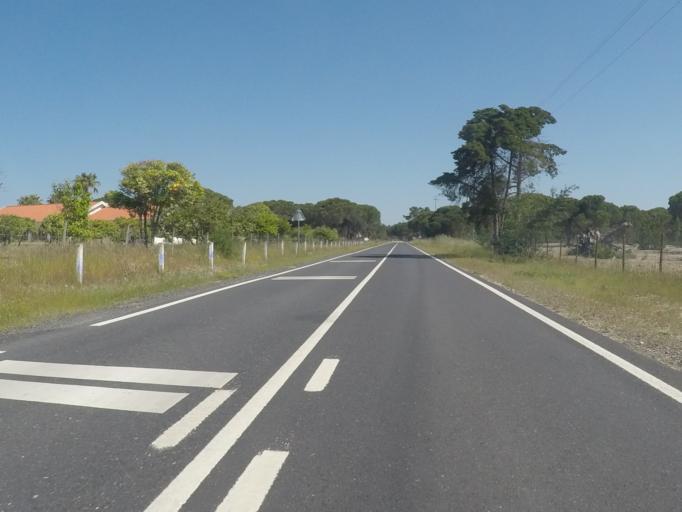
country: PT
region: Setubal
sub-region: Grandola
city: Grandola
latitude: 38.2697
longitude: -8.7272
